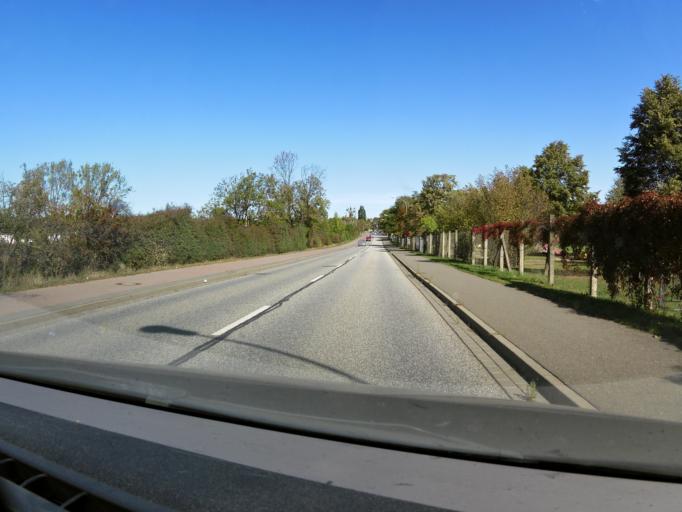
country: DE
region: Saxony-Anhalt
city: Quedlinburg
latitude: 51.7750
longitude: 11.1399
